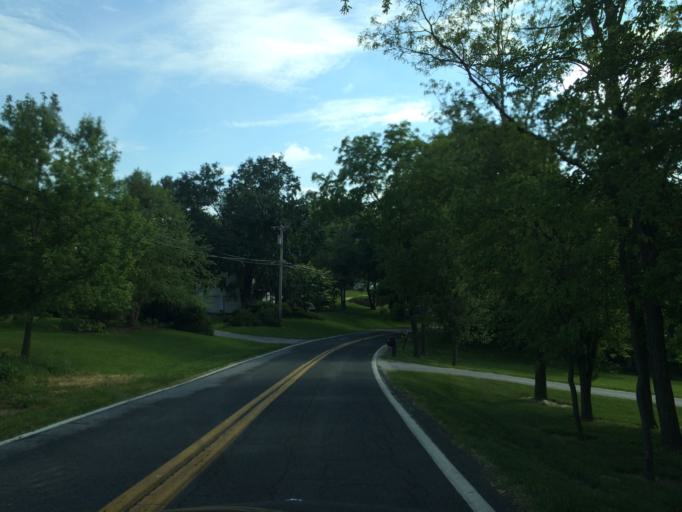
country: US
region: Maryland
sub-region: Carroll County
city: Eldersburg
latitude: 39.4868
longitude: -76.9764
